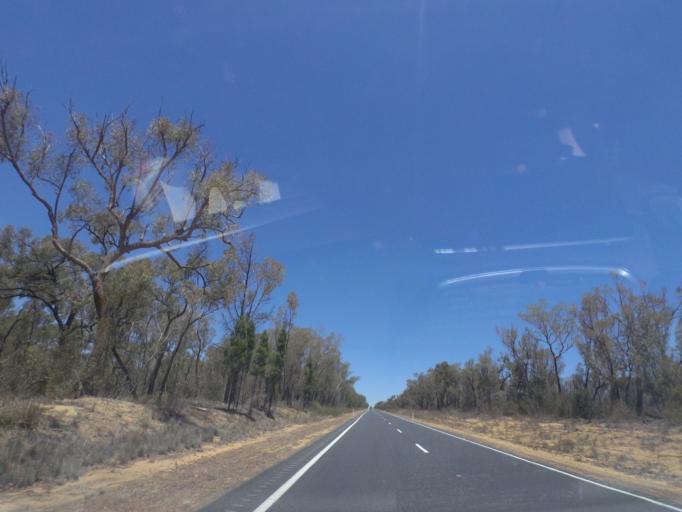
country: AU
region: New South Wales
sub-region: Warrumbungle Shire
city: Coonabarabran
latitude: -30.9509
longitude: 149.4214
